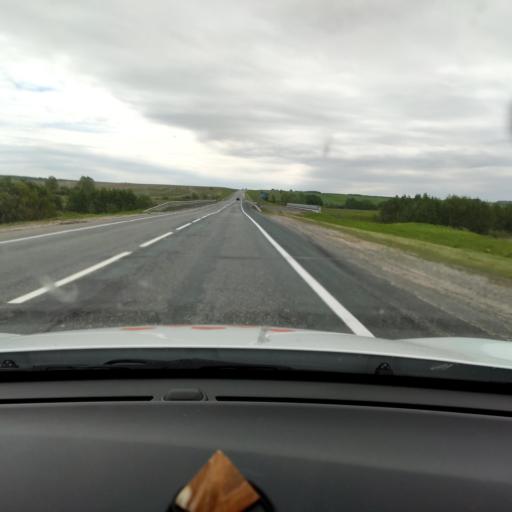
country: RU
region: Tatarstan
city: Laishevo
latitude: 55.5198
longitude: 49.7994
